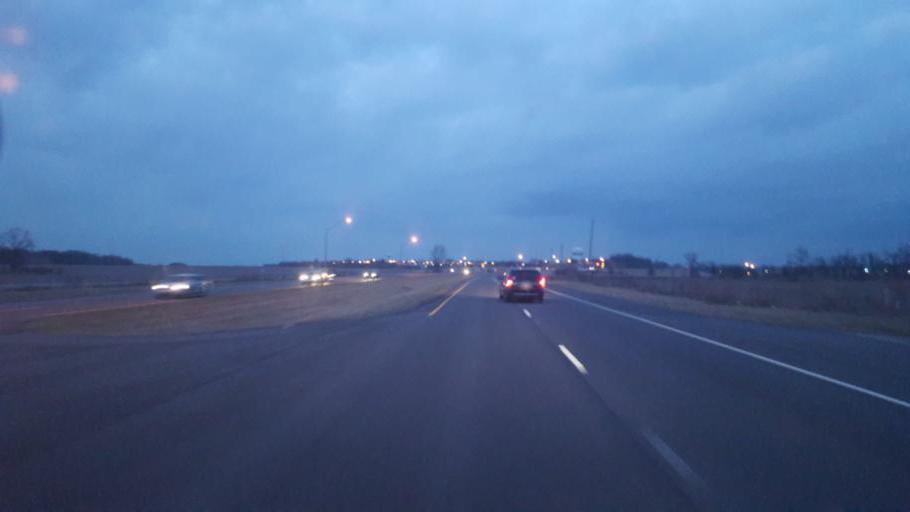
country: US
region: Ohio
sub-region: Ross County
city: Chillicothe
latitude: 39.3829
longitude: -82.9729
